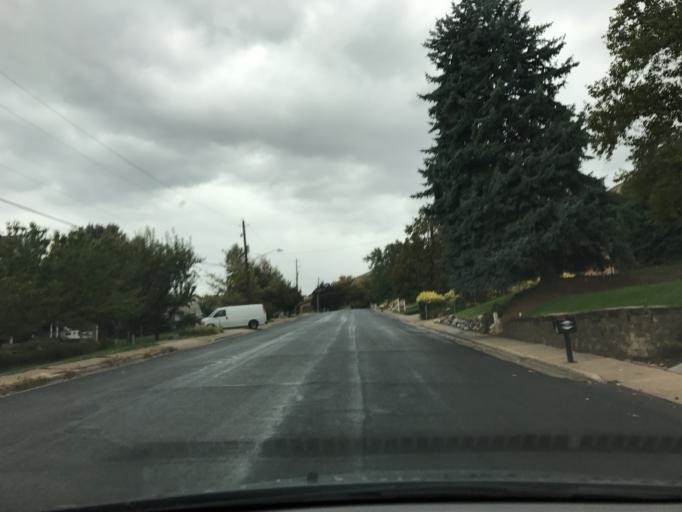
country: US
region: Utah
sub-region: Davis County
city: Farmington
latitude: 40.9970
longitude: -111.8942
